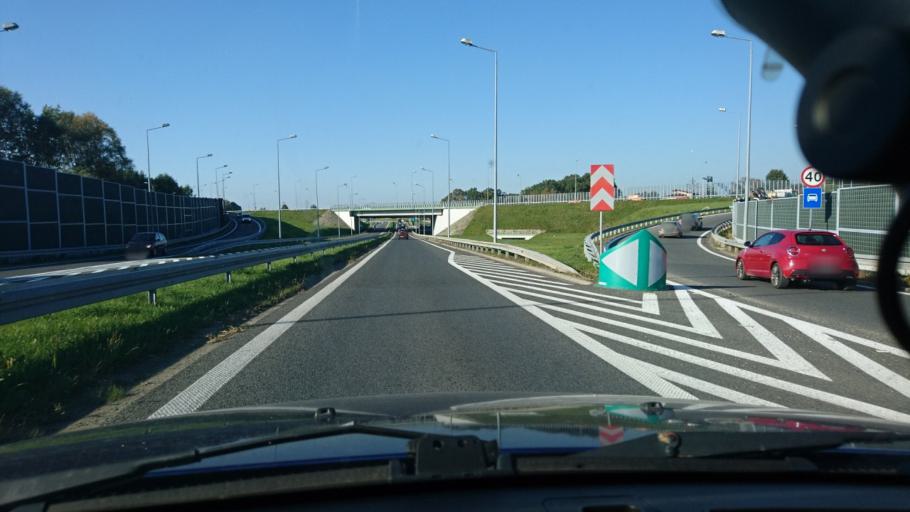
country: PL
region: Silesian Voivodeship
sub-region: Bielsko-Biala
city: Bielsko-Biala
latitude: 49.8429
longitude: 19.0690
